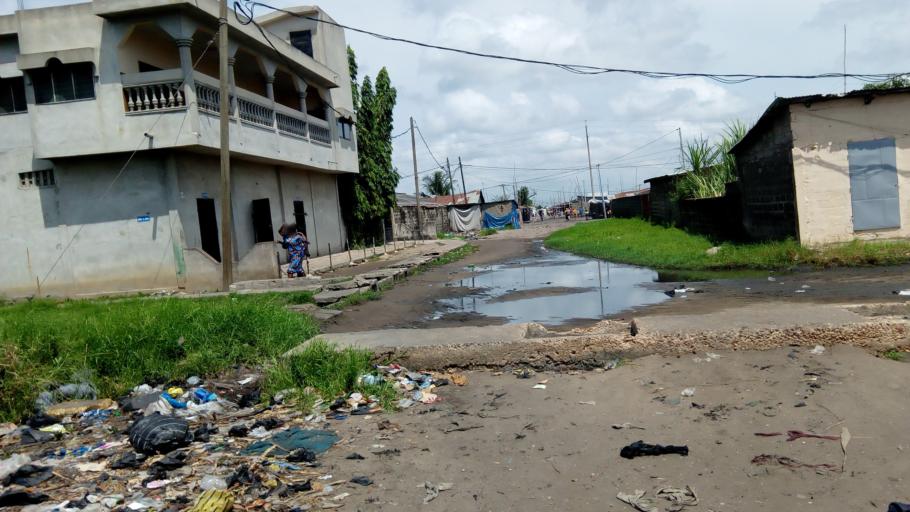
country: BJ
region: Littoral
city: Cotonou
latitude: 6.3875
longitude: 2.4330
